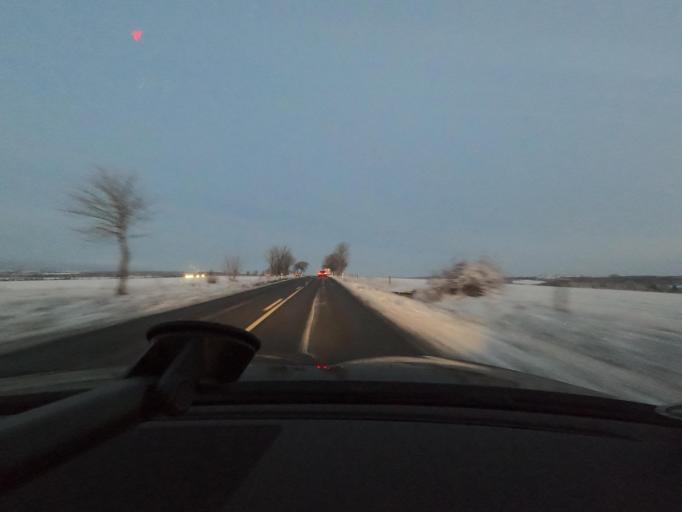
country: DE
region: Thuringia
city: Muehlhausen
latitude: 51.2657
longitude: 10.4311
